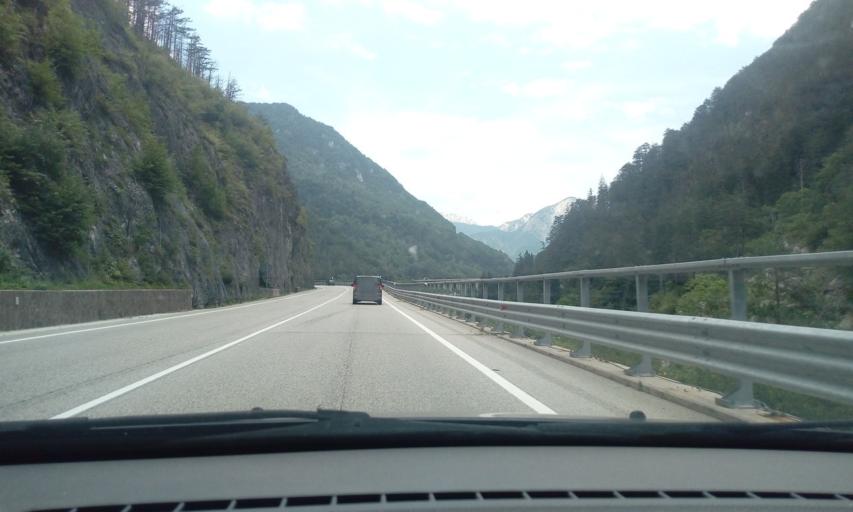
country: IT
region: Friuli Venezia Giulia
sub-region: Provincia di Udine
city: Dogna
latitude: 46.4680
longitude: 13.2937
